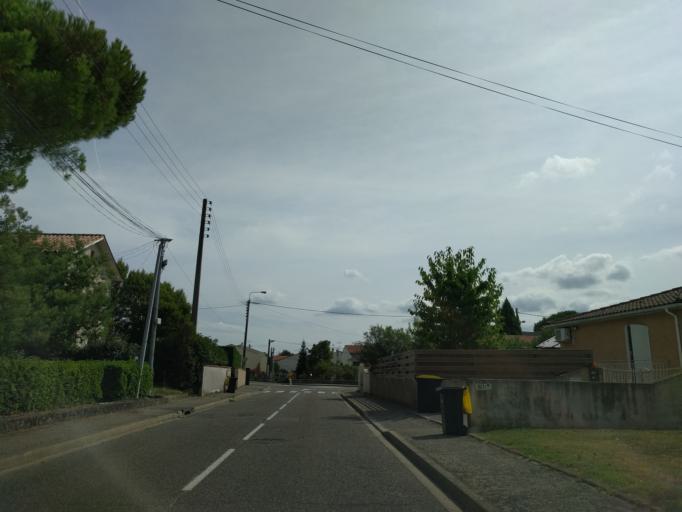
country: FR
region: Aquitaine
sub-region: Departement du Lot-et-Garonne
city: Agen
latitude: 44.1899
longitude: 0.6257
